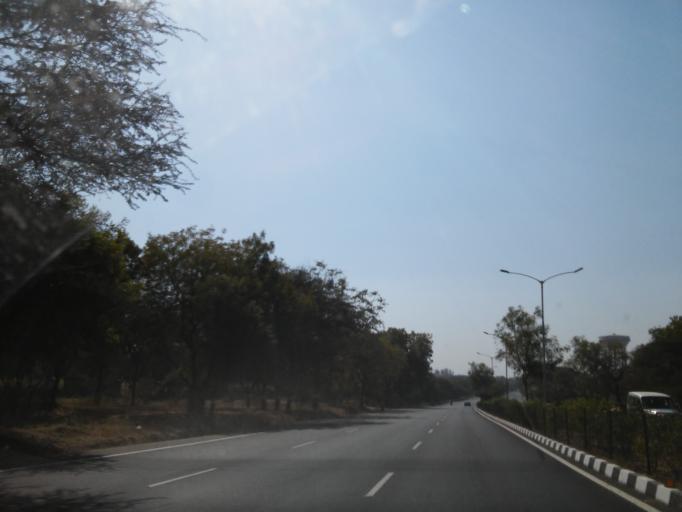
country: IN
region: Gujarat
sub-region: Gandhinagar
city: Ghandinagar
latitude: 23.2122
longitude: 72.6680
